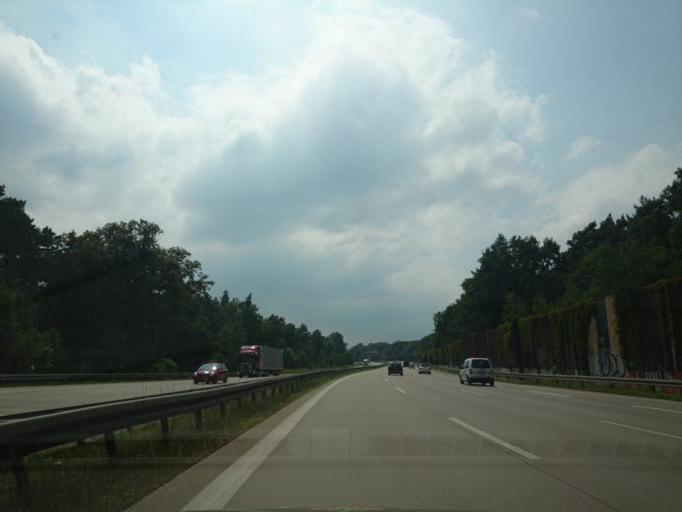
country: DE
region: Berlin
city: Wannsee
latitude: 52.3667
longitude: 13.1475
